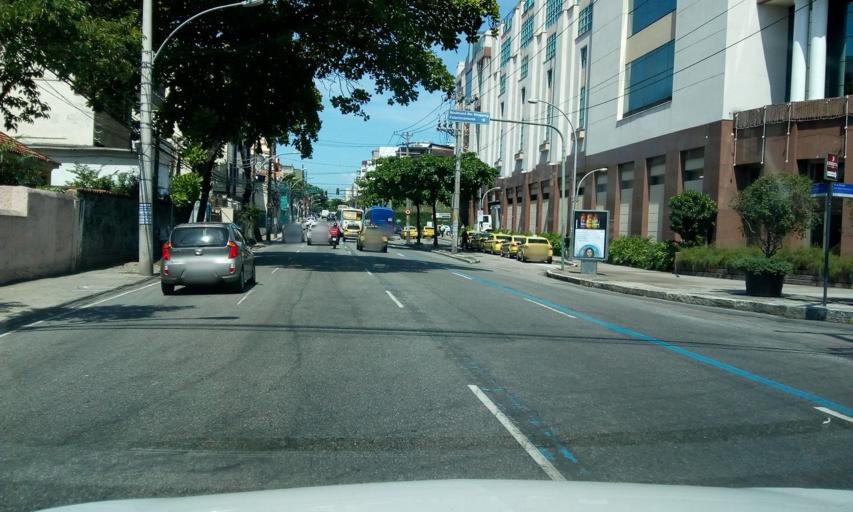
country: BR
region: Rio de Janeiro
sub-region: Rio De Janeiro
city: Rio de Janeiro
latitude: -22.9186
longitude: -43.2510
